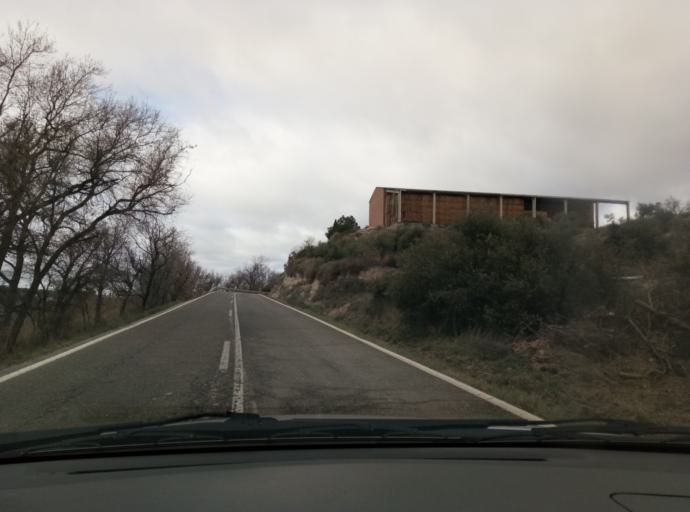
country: ES
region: Catalonia
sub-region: Provincia de Lleida
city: Nalec
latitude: 41.5613
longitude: 1.0857
